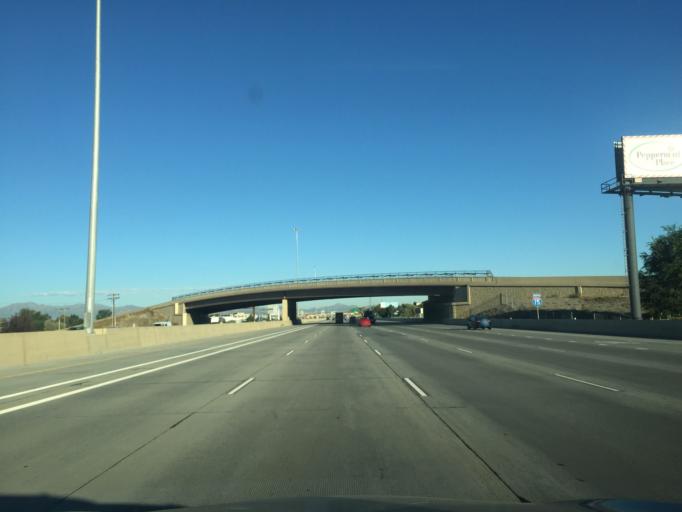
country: US
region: Utah
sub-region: Utah County
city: American Fork
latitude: 40.3545
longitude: -111.7758
